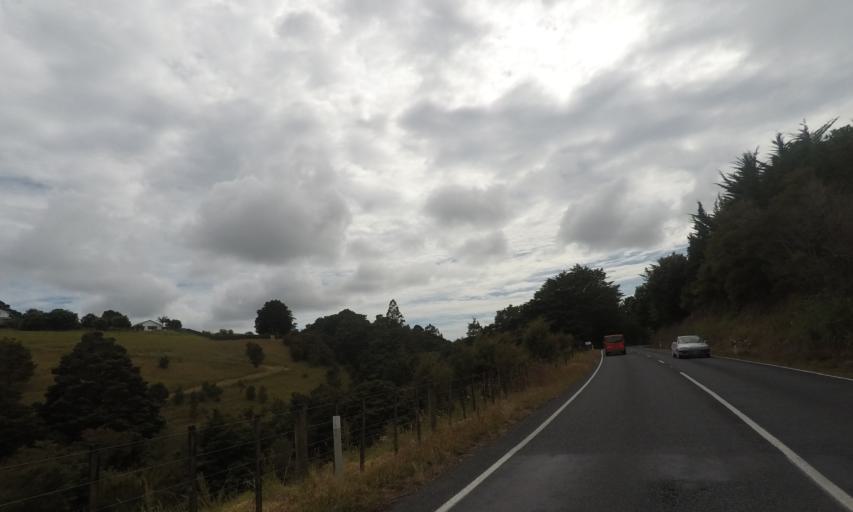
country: NZ
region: Northland
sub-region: Whangarei
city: Whangarei
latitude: -35.7654
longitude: 174.4612
